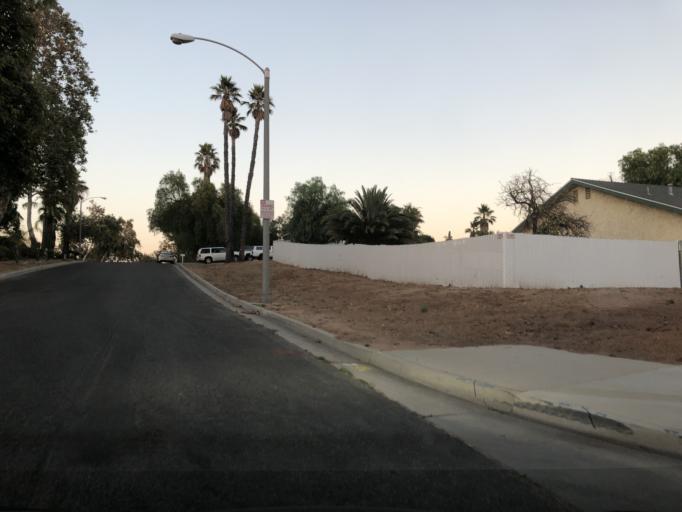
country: US
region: California
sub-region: Riverside County
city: Pedley
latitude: 33.9516
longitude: -117.4967
